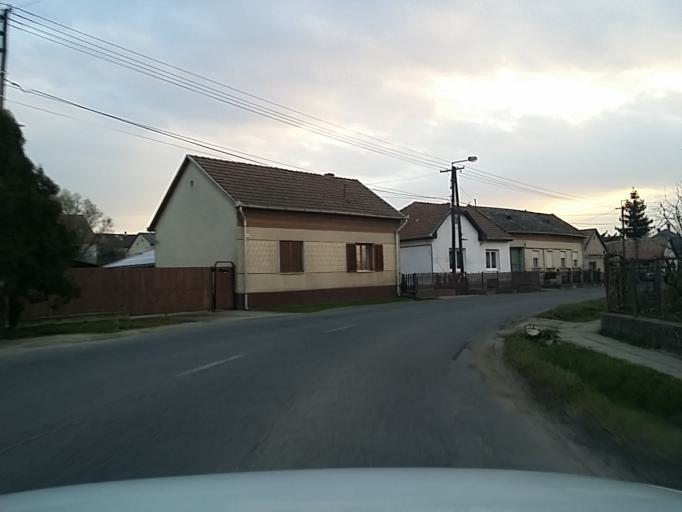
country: HU
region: Nograd
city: Batonyterenye
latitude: 47.9888
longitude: 19.8411
